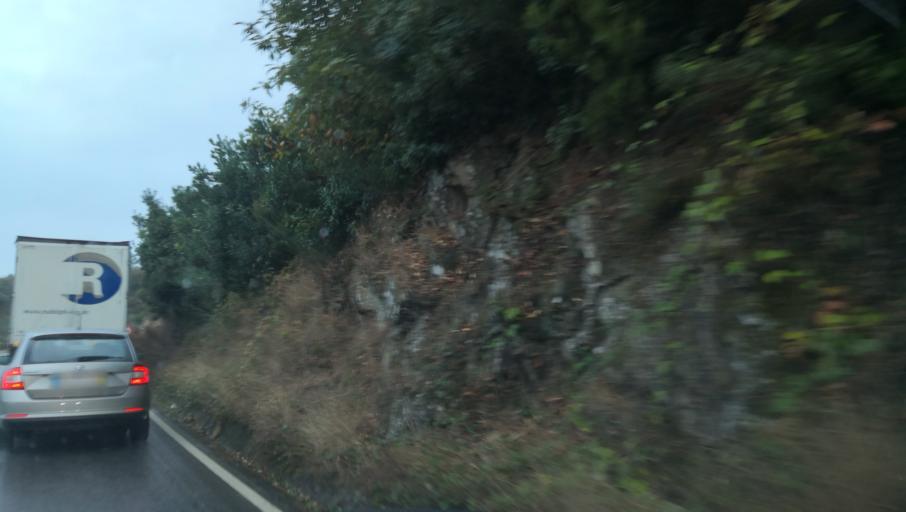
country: PT
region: Vila Real
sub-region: Vila Real
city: Vila Real
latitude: 41.2433
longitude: -7.7254
